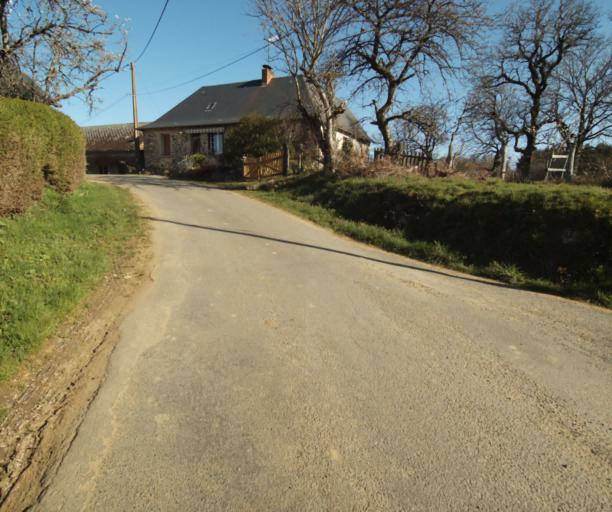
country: FR
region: Limousin
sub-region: Departement de la Correze
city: Saint-Clement
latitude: 45.3751
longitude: 1.6565
